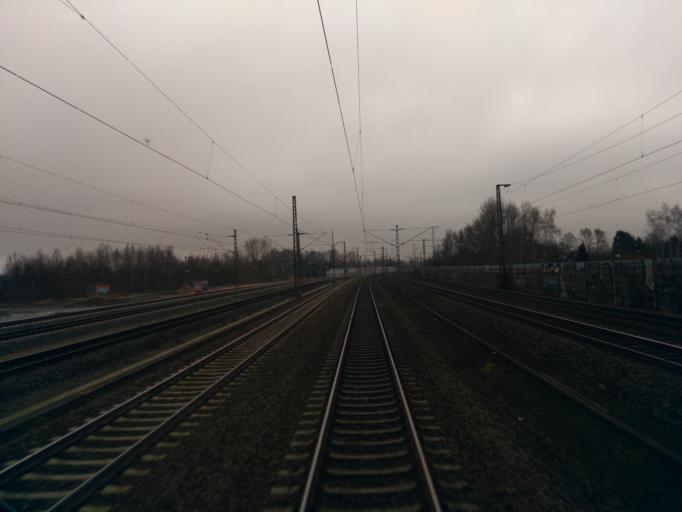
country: DE
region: Hamburg
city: Kleiner Grasbrook
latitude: 53.5090
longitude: 10.0083
